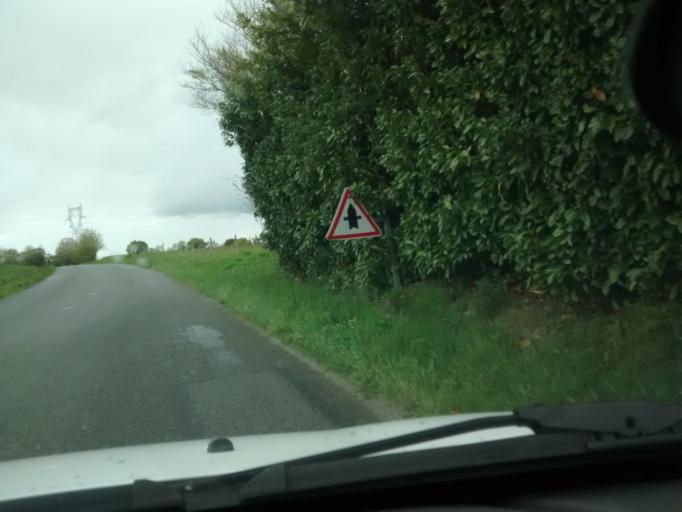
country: FR
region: Brittany
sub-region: Departement d'Ille-et-Vilaine
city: Nouvoitou
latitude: 48.0691
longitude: -1.5322
